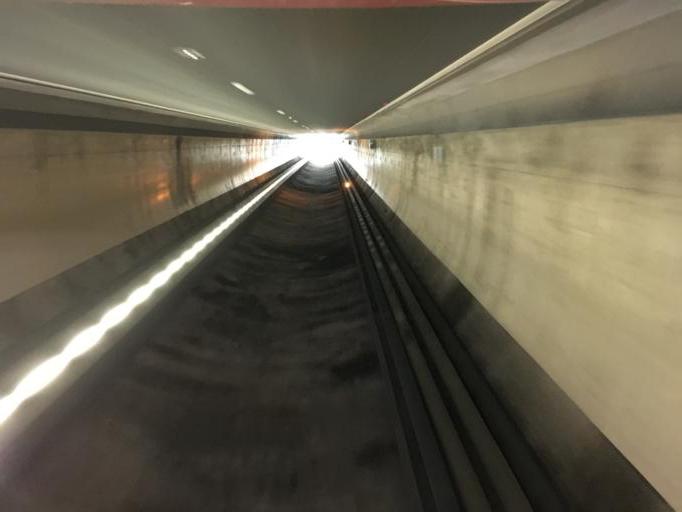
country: GB
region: Wales
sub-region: Monmouthshire
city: Monmouth
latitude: 51.8040
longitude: -2.7172
